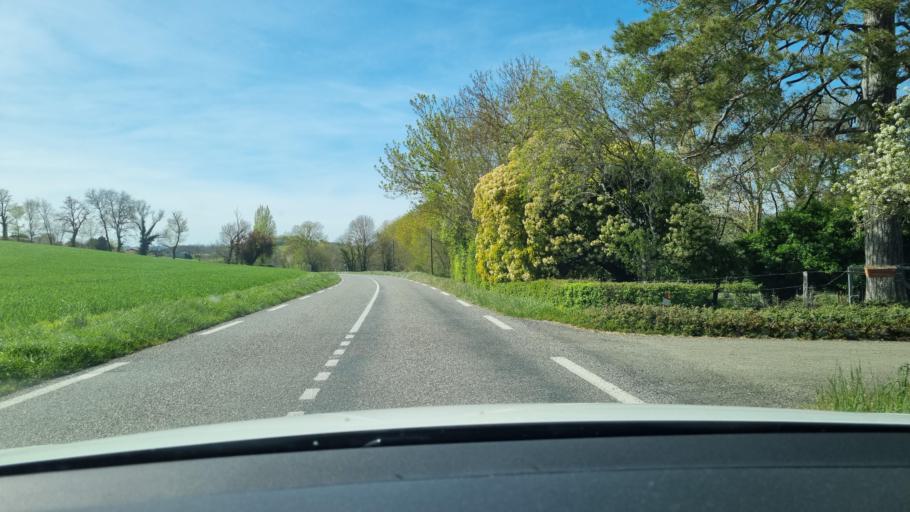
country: FR
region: Midi-Pyrenees
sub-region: Departement du Gers
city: Samatan
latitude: 43.4896
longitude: 1.0137
